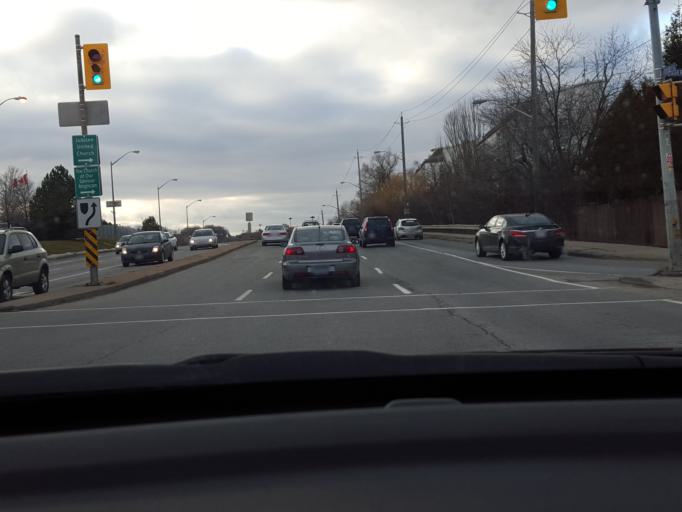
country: CA
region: Ontario
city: Scarborough
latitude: 43.7409
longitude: -79.3245
